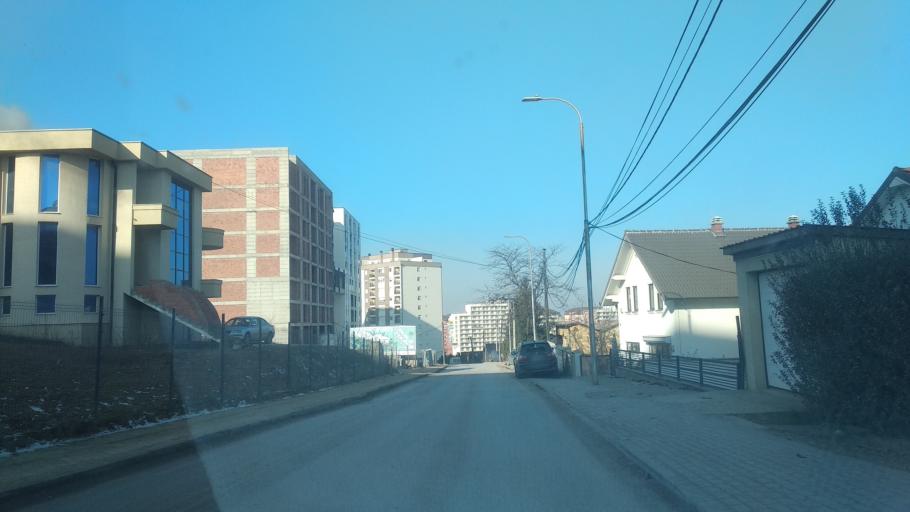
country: XK
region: Pristina
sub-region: Komuna e Prishtines
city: Pristina
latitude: 42.6392
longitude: 21.1595
